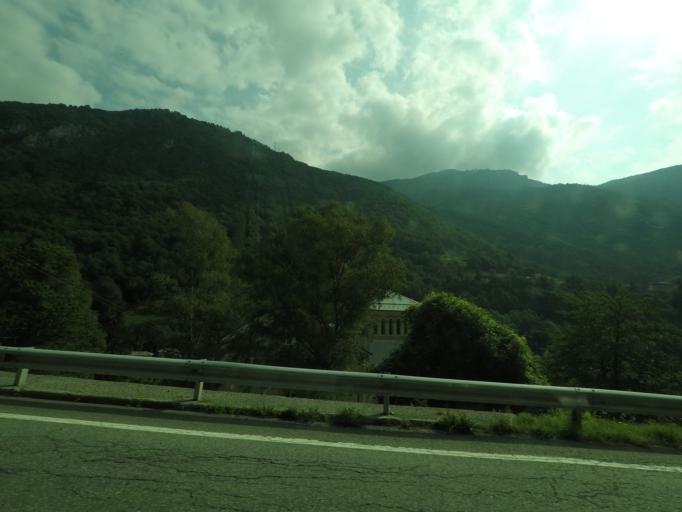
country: IT
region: Aosta Valley
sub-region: Valle d'Aosta
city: Antey-Saint-Andre
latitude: 45.7741
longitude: 7.5942
